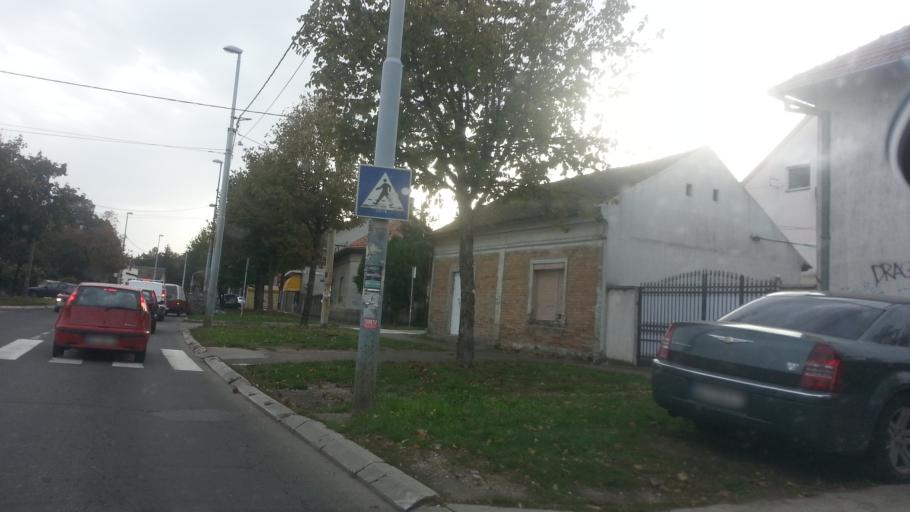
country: RS
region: Central Serbia
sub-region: Belgrade
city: Zemun
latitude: 44.8496
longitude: 20.3900
